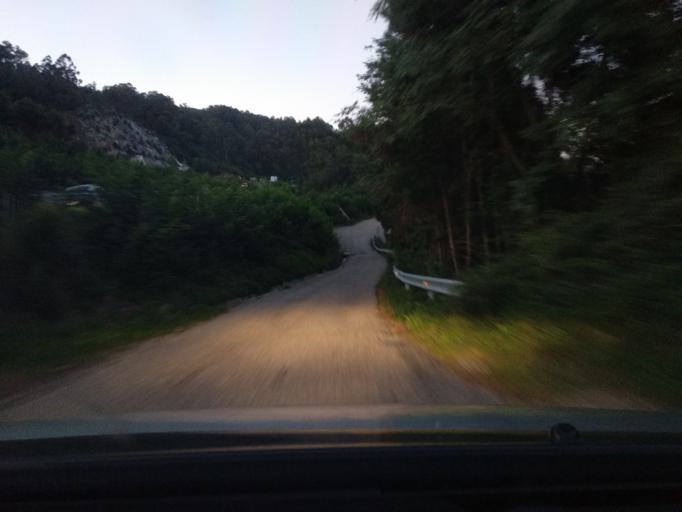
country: ES
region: Galicia
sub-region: Provincia de Pontevedra
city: Moana
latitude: 42.2874
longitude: -8.7531
